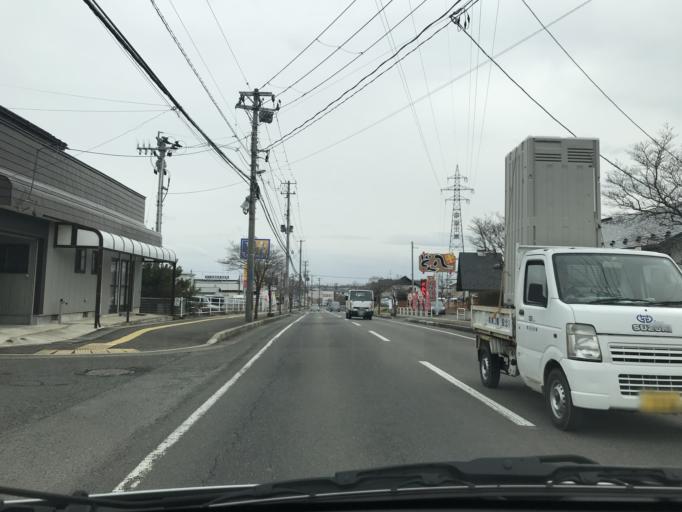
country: JP
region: Iwate
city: Hanamaki
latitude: 39.4073
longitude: 141.1073
